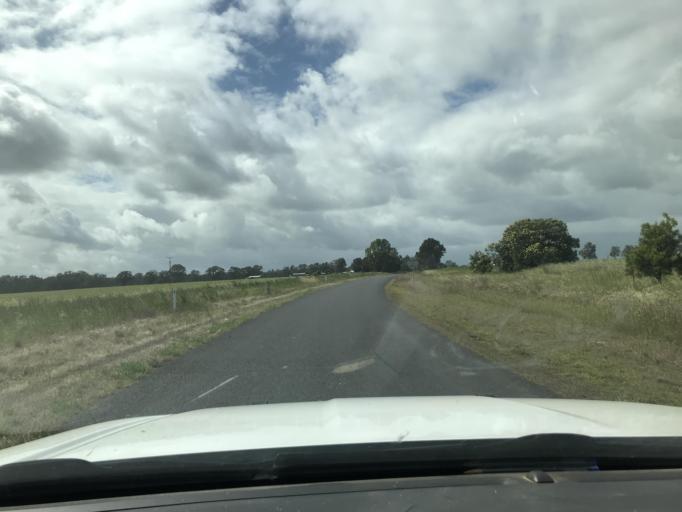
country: AU
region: South Australia
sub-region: Wattle Range
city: Penola
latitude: -37.1465
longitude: 141.3948
